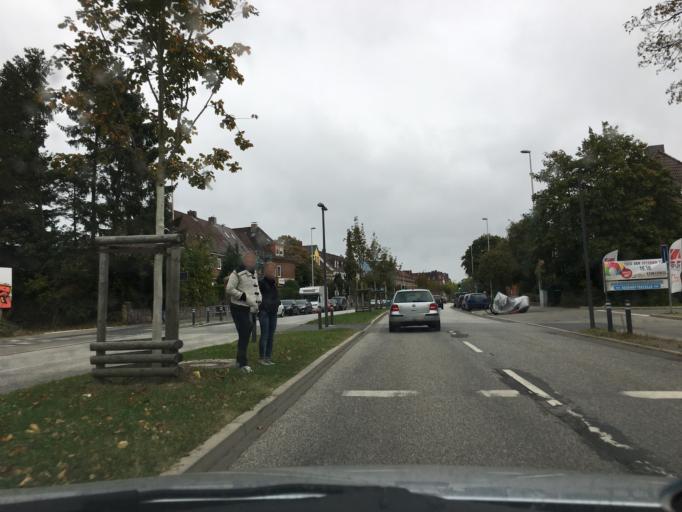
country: DE
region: Schleswig-Holstein
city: Kiel
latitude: 54.3265
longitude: 10.1089
